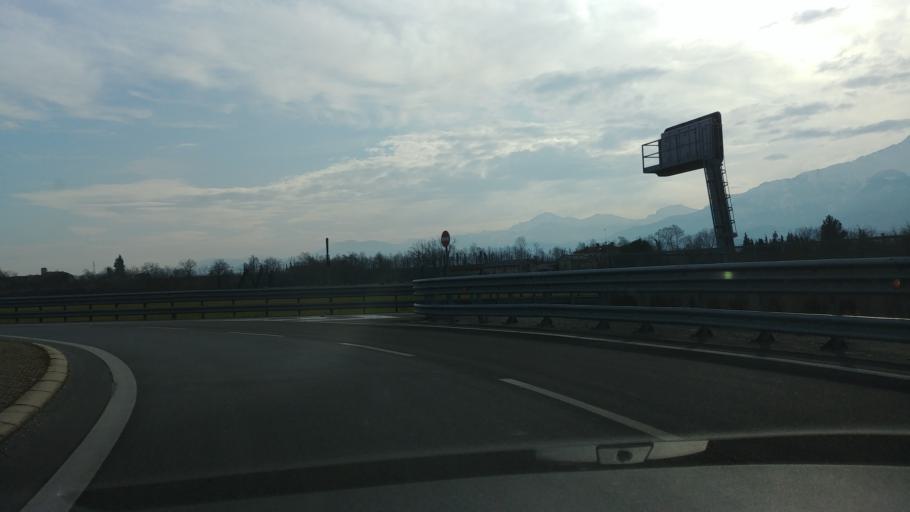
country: IT
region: Piedmont
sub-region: Provincia di Cuneo
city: Cuneo
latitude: 44.3681
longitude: 7.5520
